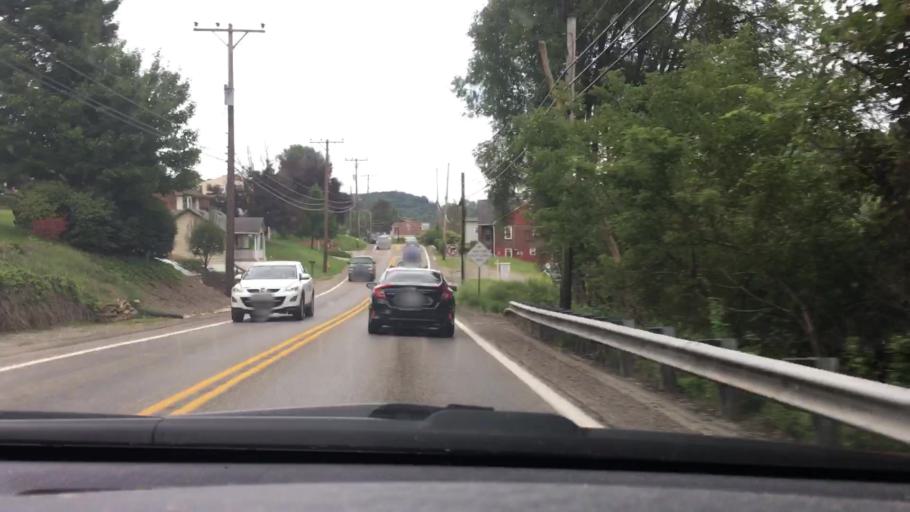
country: US
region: Pennsylvania
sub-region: Allegheny County
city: Baldwin
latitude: 40.3307
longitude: -79.9938
